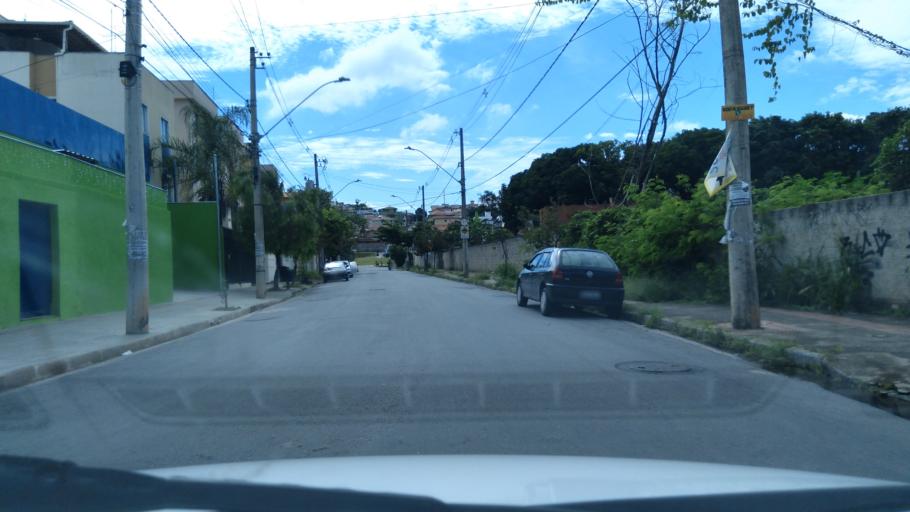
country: BR
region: Minas Gerais
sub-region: Belo Horizonte
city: Belo Horizonte
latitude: -19.8740
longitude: -43.9207
